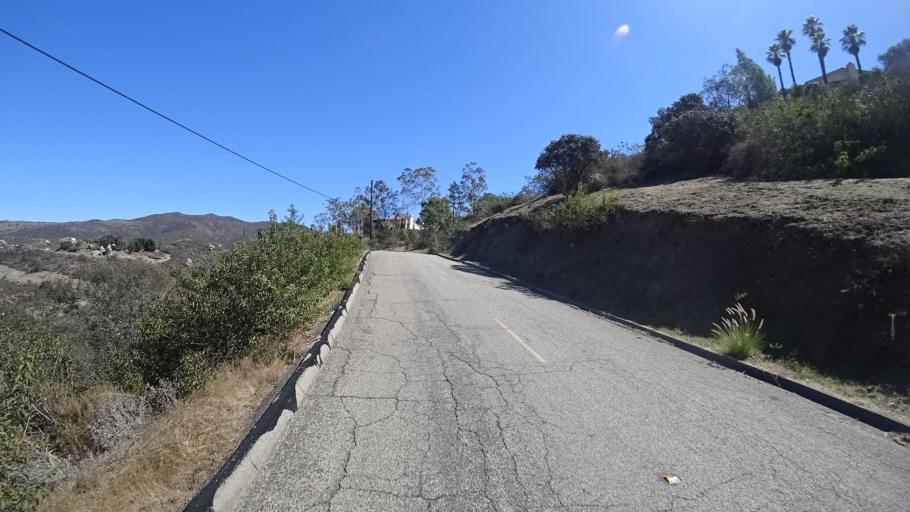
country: US
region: California
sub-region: San Diego County
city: Jamul
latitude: 32.7390
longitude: -116.8789
